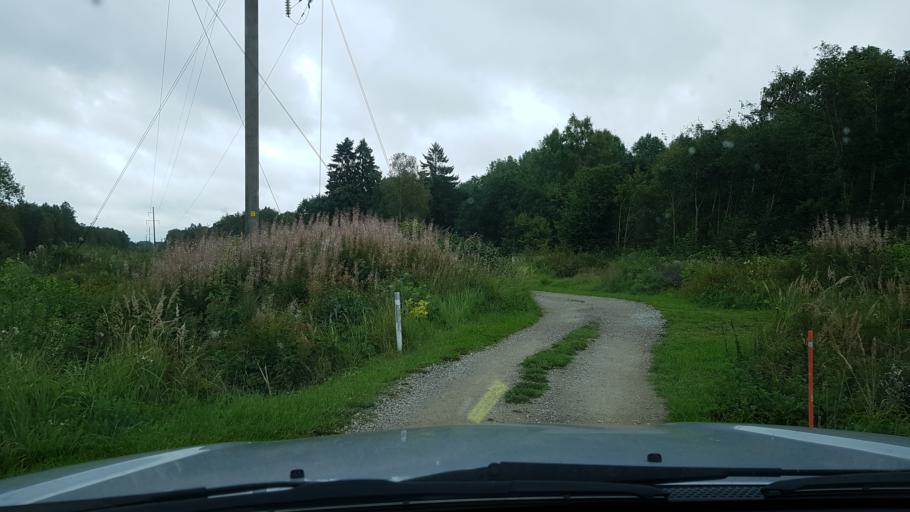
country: EE
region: Harju
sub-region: Rae vald
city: Jueri
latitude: 59.3536
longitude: 24.9225
